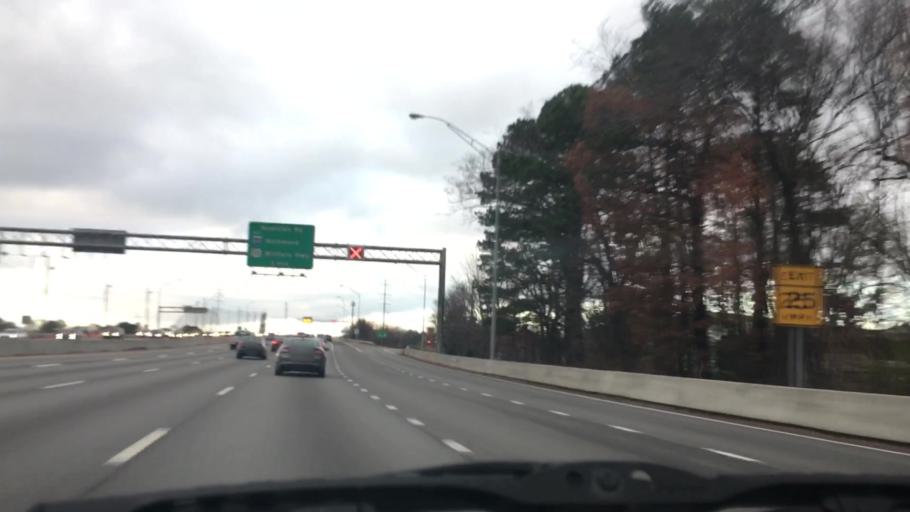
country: US
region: Virginia
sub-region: City of Chesapeake
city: Chesapeake
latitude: 36.8370
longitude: -76.1565
